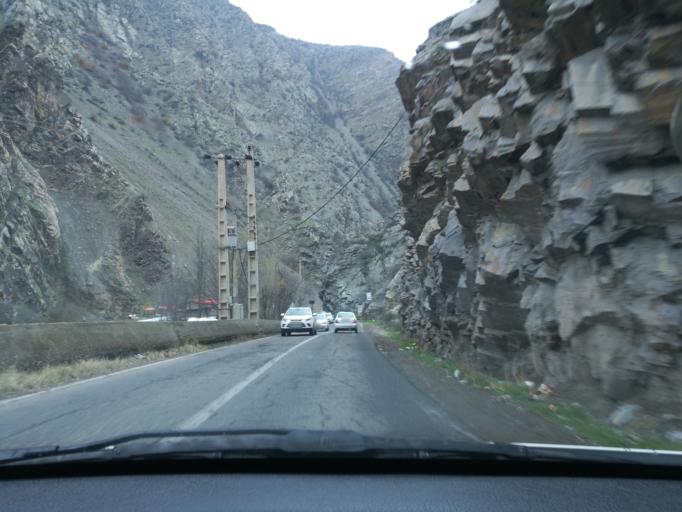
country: IR
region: Mazandaran
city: Chalus
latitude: 36.3011
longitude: 51.2483
